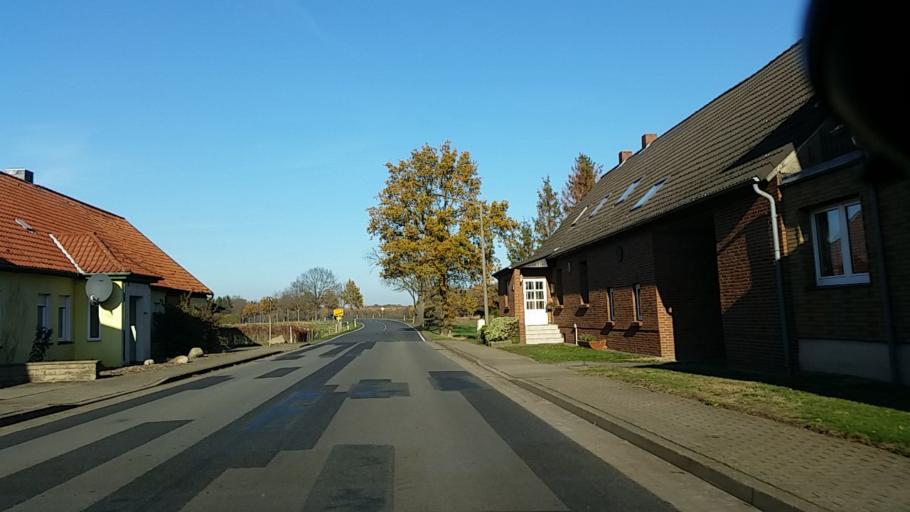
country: DE
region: Saxony-Anhalt
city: Jubar
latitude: 52.6507
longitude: 10.8615
